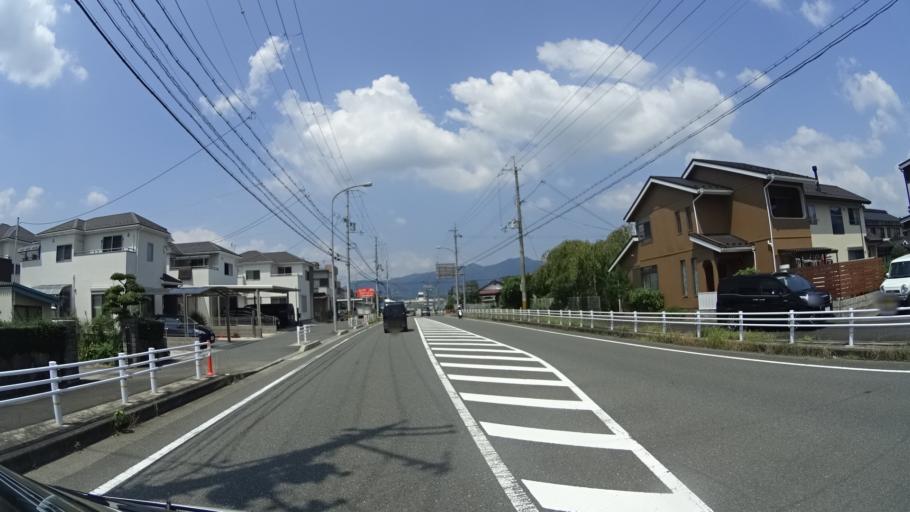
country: JP
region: Kyoto
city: Fukuchiyama
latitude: 35.2852
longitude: 135.1377
